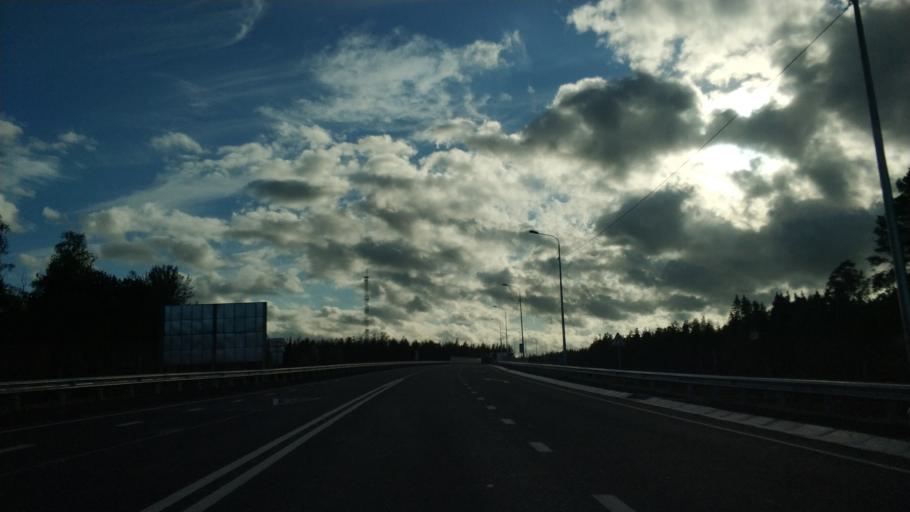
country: RU
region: Leningrad
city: Priozersk
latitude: 60.8454
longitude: 30.1402
